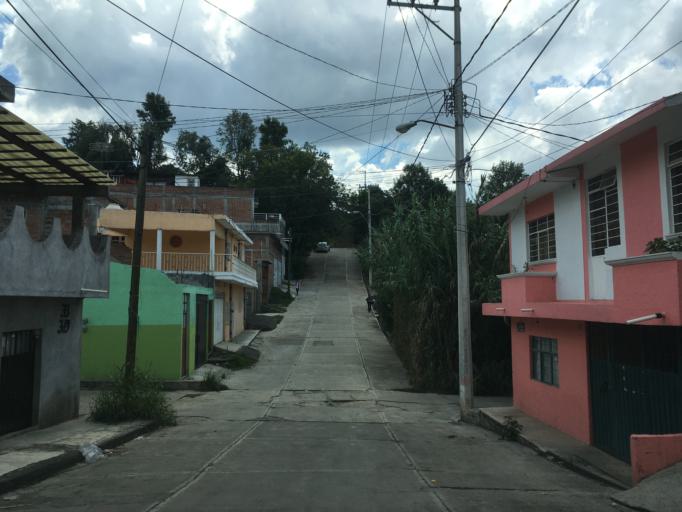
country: MX
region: Michoacan
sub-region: Morelia
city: Morelos
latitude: 19.6478
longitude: -101.2402
